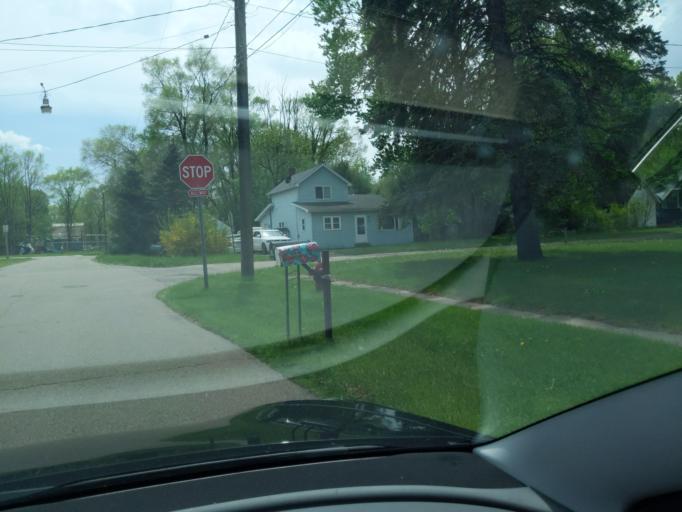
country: US
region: Michigan
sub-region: Ingham County
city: Stockbridge
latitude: 42.4469
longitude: -84.1789
